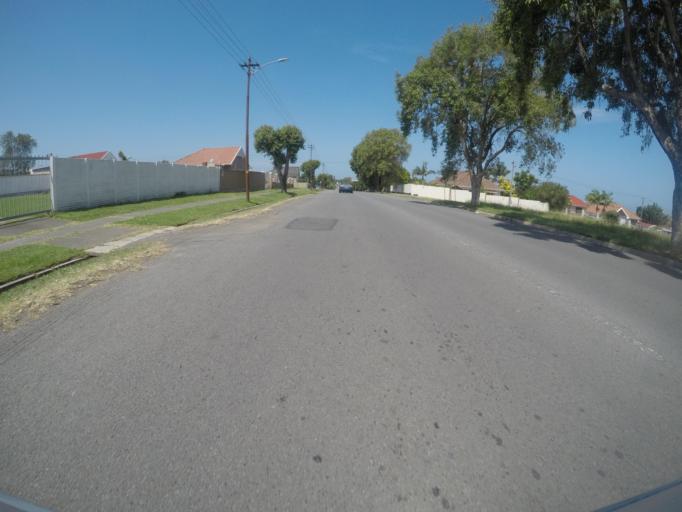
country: ZA
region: Eastern Cape
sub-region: Buffalo City Metropolitan Municipality
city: East London
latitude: -32.9805
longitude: 27.8893
